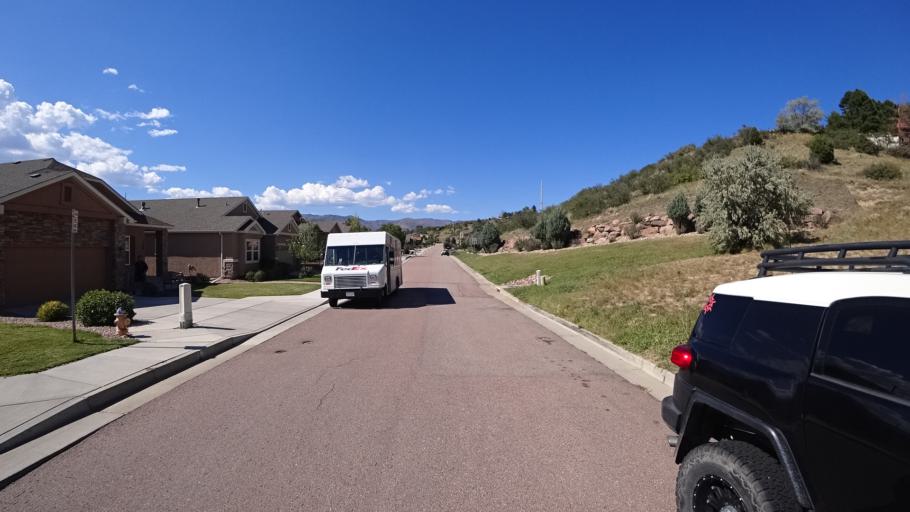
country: US
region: Colorado
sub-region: El Paso County
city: Colorado Springs
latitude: 38.8579
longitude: -104.8495
